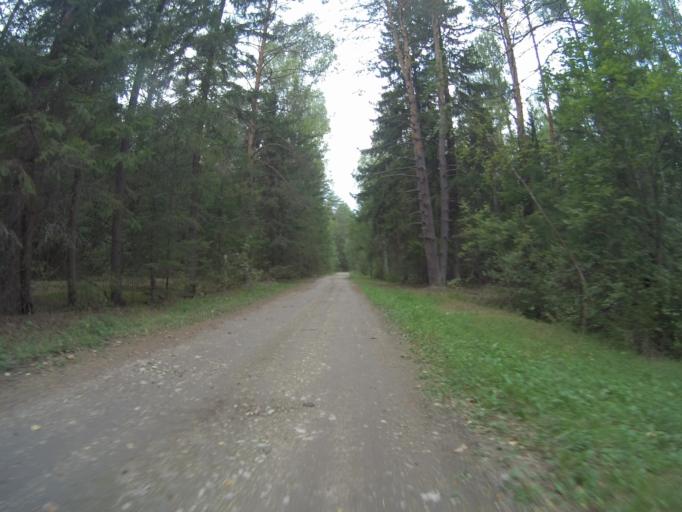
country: RU
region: Vladimir
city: Golovino
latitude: 55.9386
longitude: 40.4762
